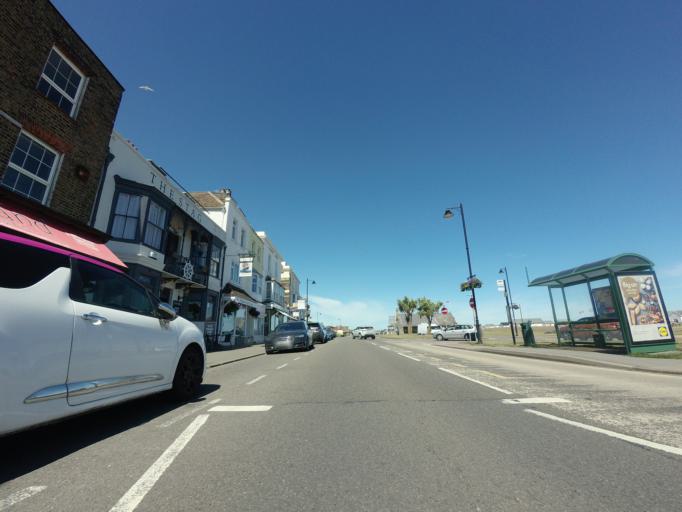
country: GB
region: England
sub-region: Kent
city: Deal
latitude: 51.2126
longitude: 1.4025
